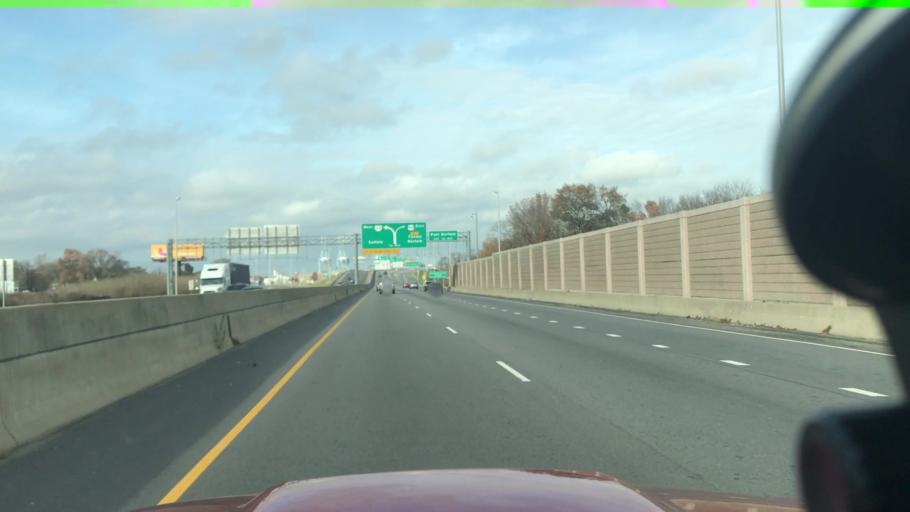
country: US
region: Virginia
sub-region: City of Portsmouth
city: Portsmouth
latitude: 36.8399
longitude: -76.3291
